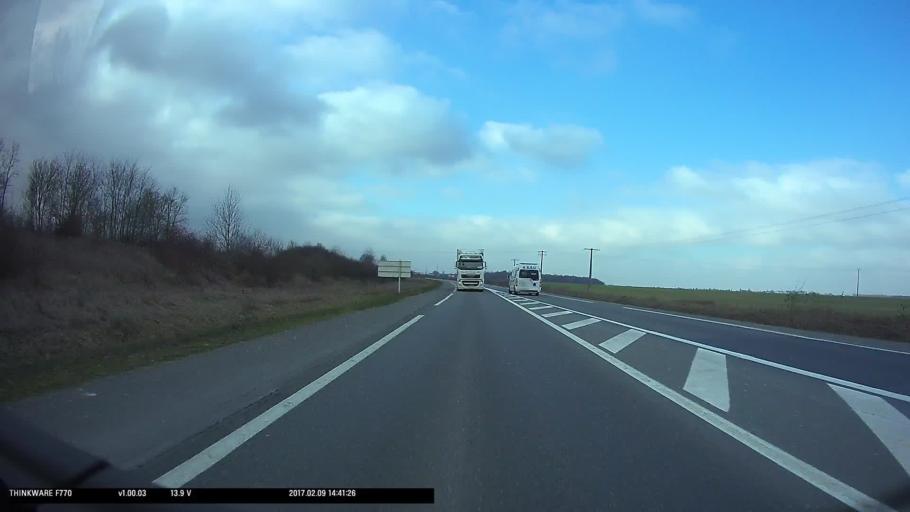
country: FR
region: Centre
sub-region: Departement du Cher
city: Trouy
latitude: 47.0351
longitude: 2.3708
